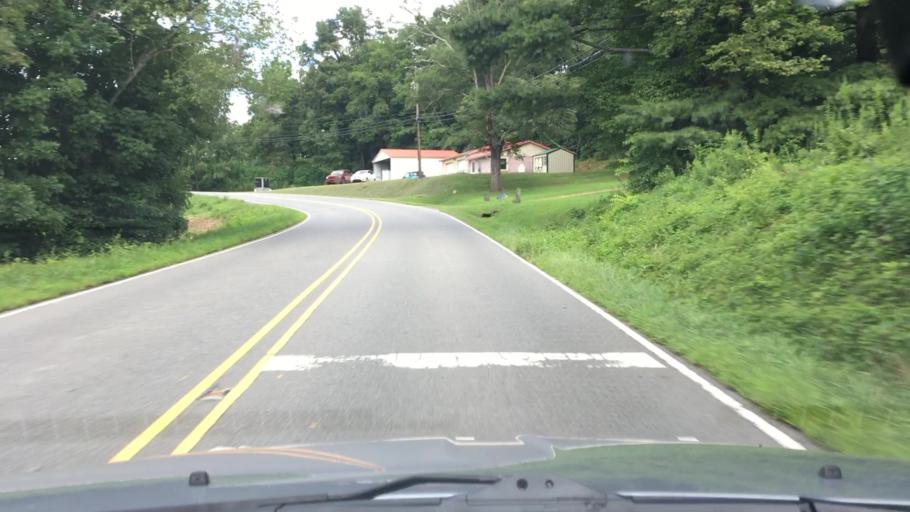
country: US
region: North Carolina
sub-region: Yancey County
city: Burnsville
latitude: 35.8369
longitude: -82.1882
